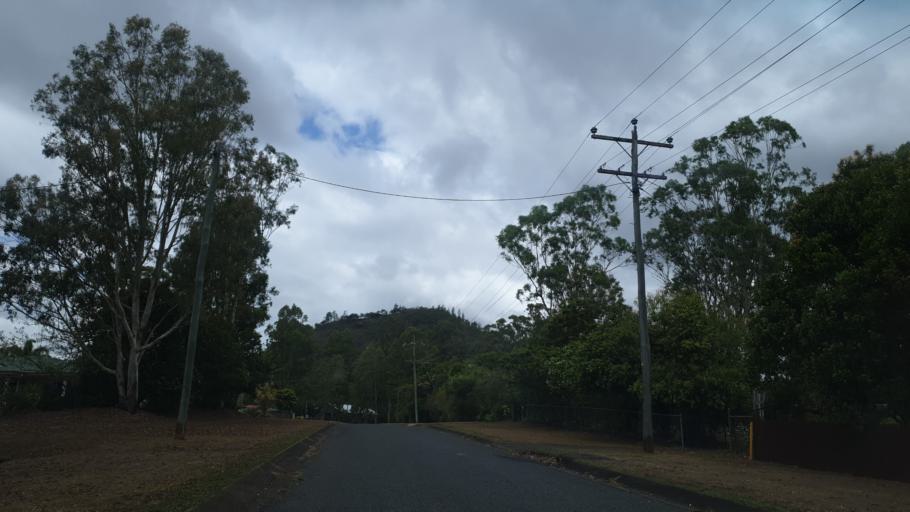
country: AU
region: Queensland
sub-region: Tablelands
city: Tolga
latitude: -17.2097
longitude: 145.4399
